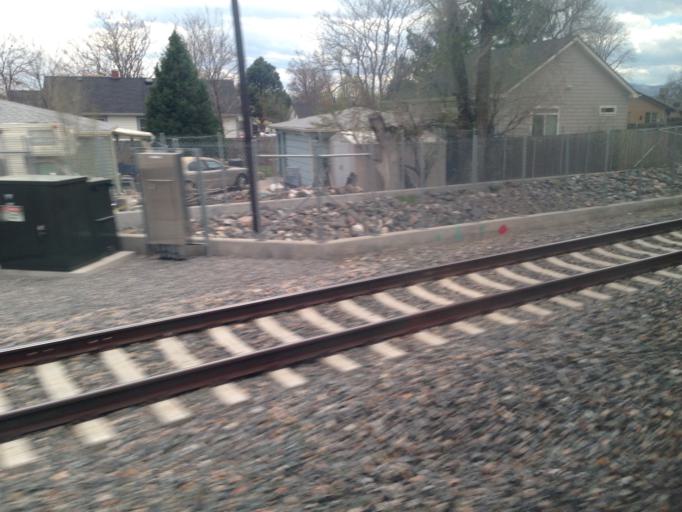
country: US
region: Colorado
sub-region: Jefferson County
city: Arvada
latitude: 39.7940
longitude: -105.1007
